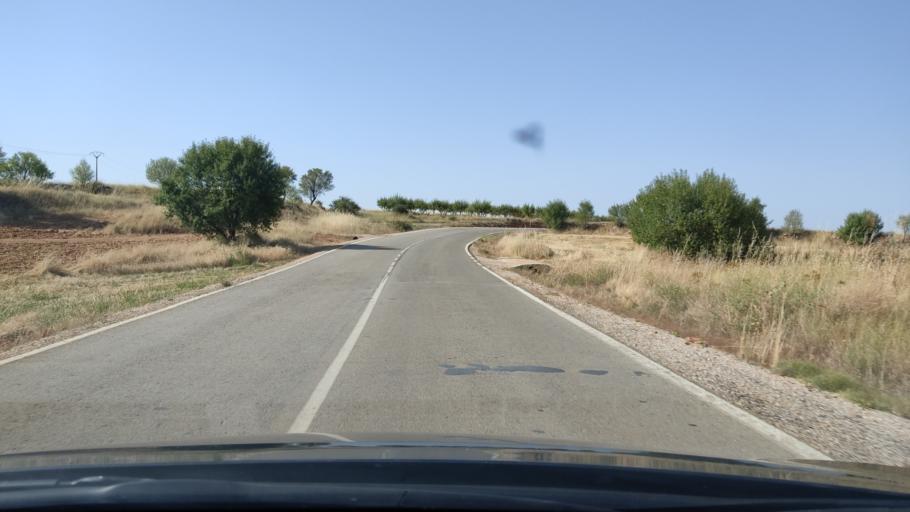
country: ES
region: Aragon
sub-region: Provincia de Teruel
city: Cucalon
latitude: 41.0819
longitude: -1.2210
